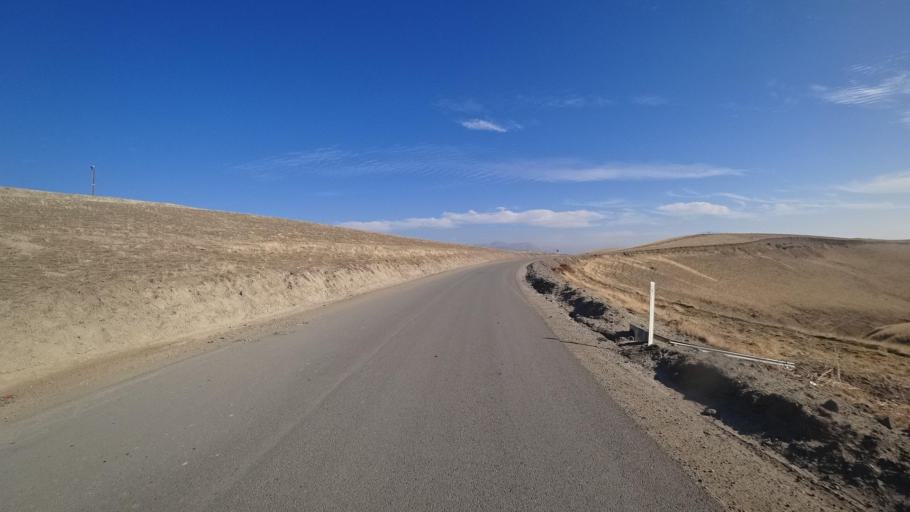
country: US
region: California
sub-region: Kern County
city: Oildale
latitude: 35.4870
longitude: -118.8772
